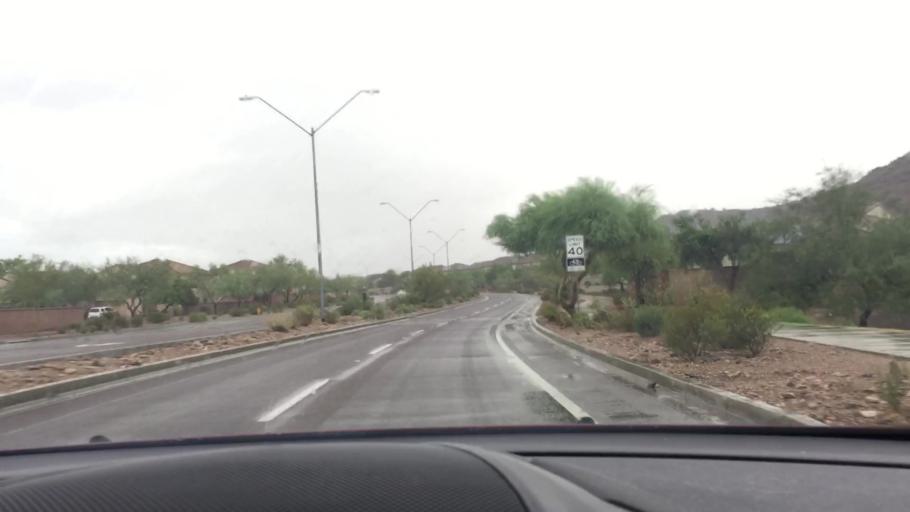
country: US
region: Arizona
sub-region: Maricopa County
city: Sun City West
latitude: 33.7328
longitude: -112.2535
